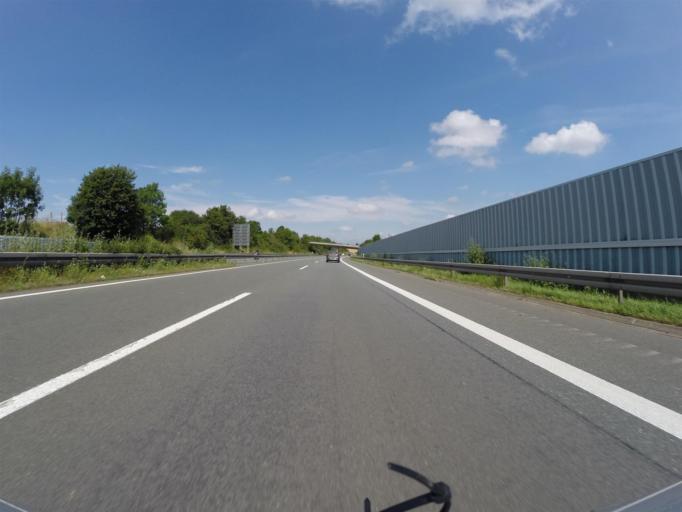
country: DE
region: North Rhine-Westphalia
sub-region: Regierungsbezirk Detmold
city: Paderborn
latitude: 51.6559
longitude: 8.7109
